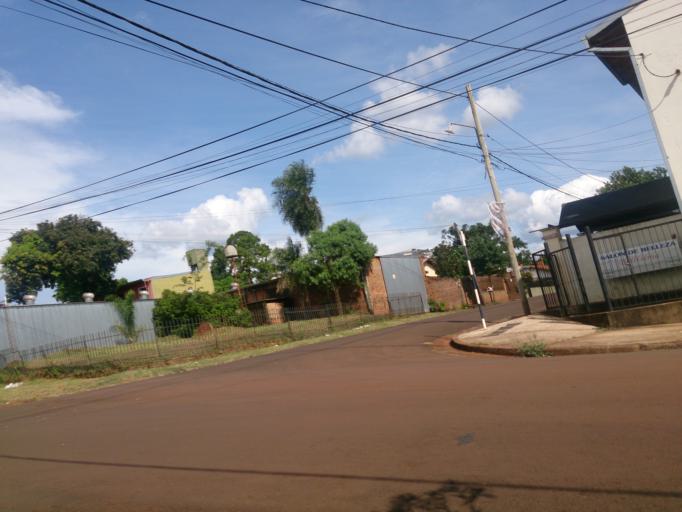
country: AR
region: Misiones
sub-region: Departamento de Obera
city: Obera
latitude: -27.4932
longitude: -55.1253
